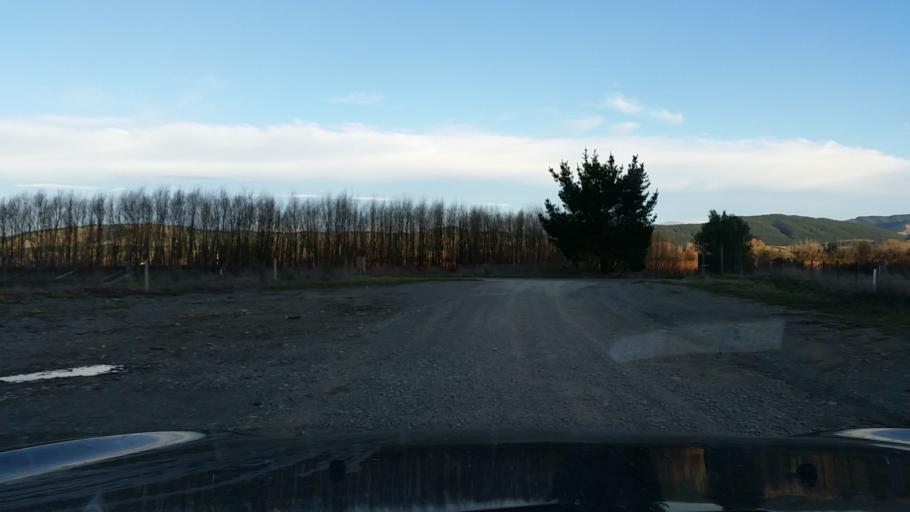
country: NZ
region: Marlborough
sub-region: Marlborough District
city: Blenheim
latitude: -41.5204
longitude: 173.5817
